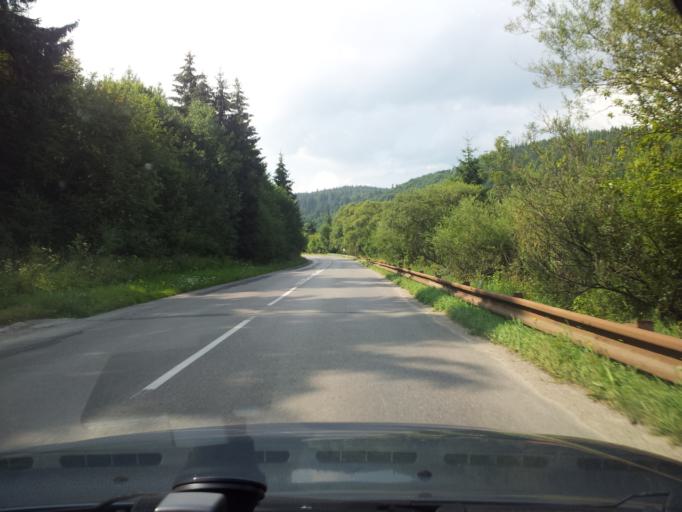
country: SK
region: Zilinsky
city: Namestovo
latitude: 49.3808
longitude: 19.3882
